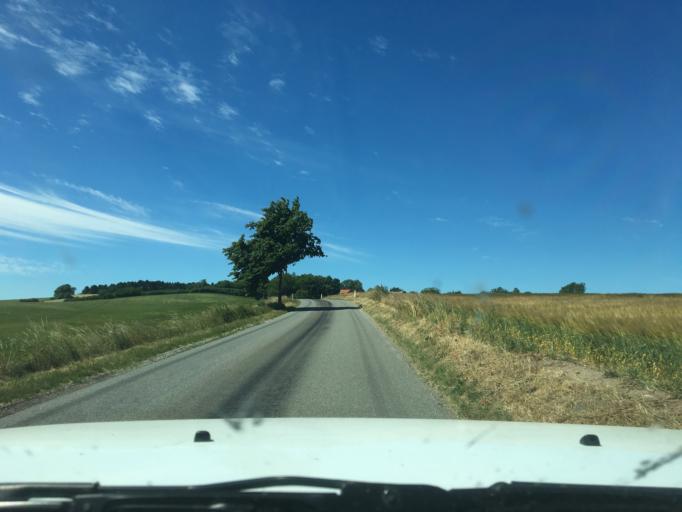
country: DK
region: Central Jutland
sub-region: Syddjurs Kommune
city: Ronde
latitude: 56.3372
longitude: 10.4115
